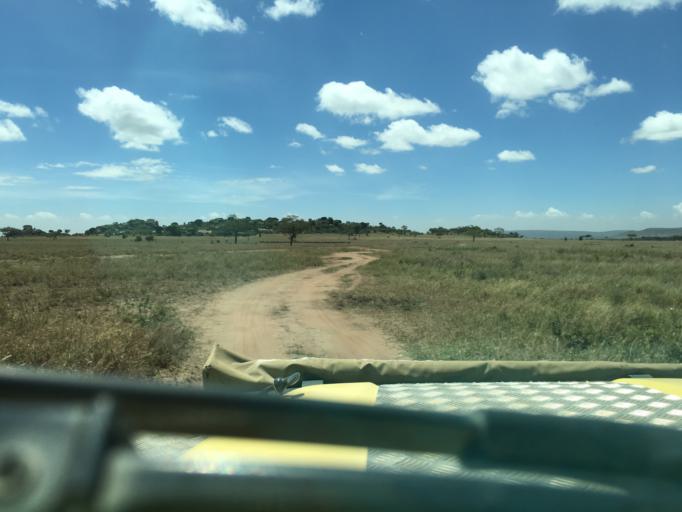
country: TZ
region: Simiyu
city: Kisesa
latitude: -2.6861
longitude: 34.7755
